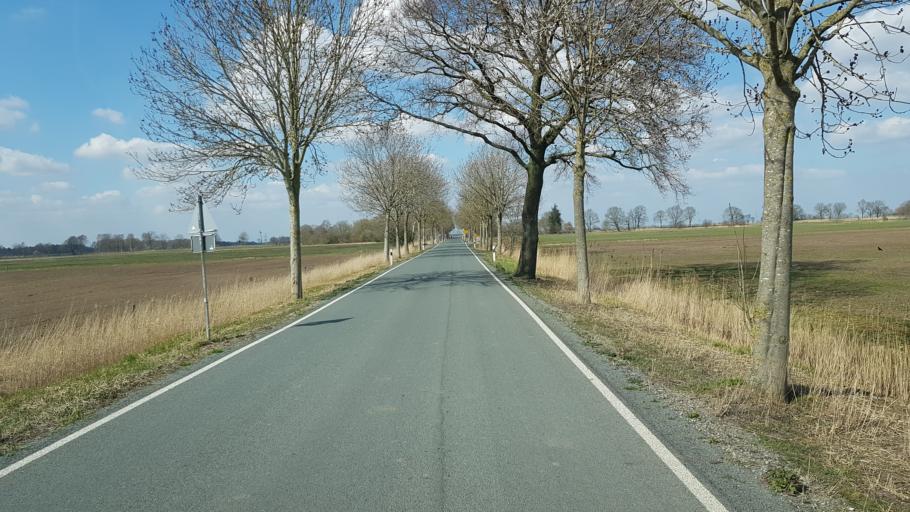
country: DE
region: Lower Saxony
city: Rastede
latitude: 53.3353
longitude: 8.2234
